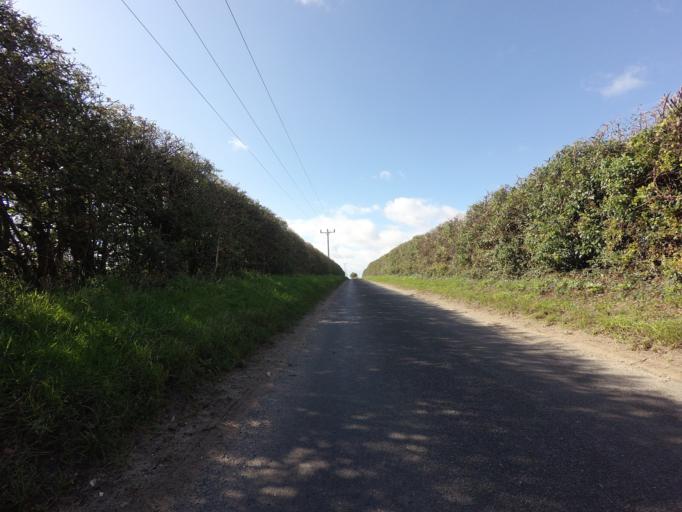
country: GB
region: England
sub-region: Norfolk
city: Hunstanton
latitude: 52.9359
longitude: 0.5942
